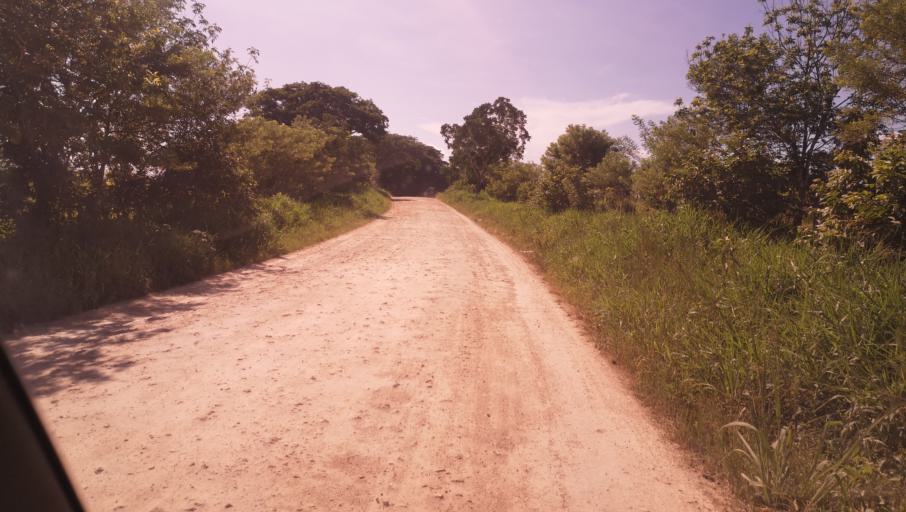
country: GT
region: Peten
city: Dolores
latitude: 16.7210
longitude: -89.3762
